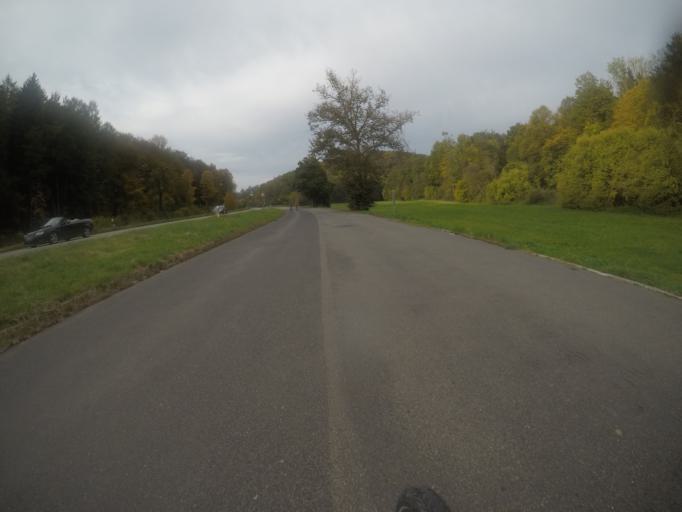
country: DE
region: Baden-Wuerttemberg
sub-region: Tuebingen Region
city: Tuebingen
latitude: 48.5469
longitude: 9.0754
